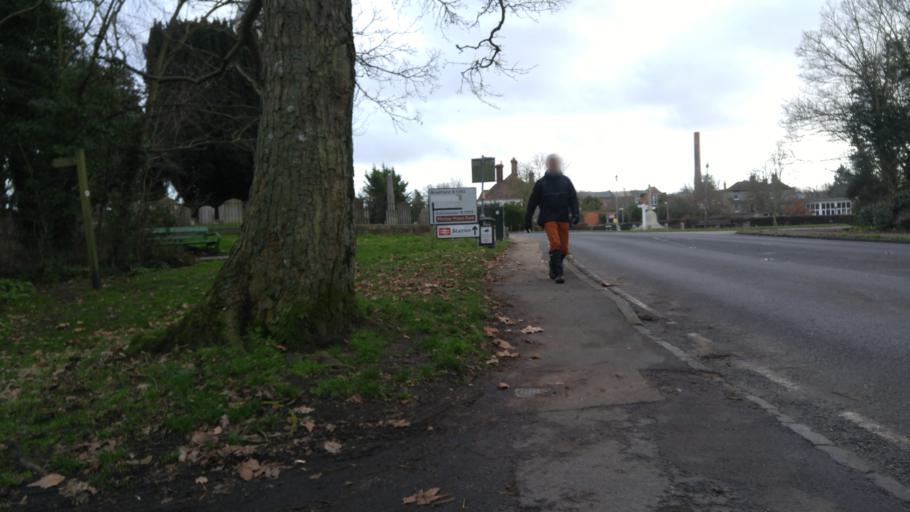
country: GB
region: England
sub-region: Essex
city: Mistley
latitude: 51.9463
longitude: 1.0767
